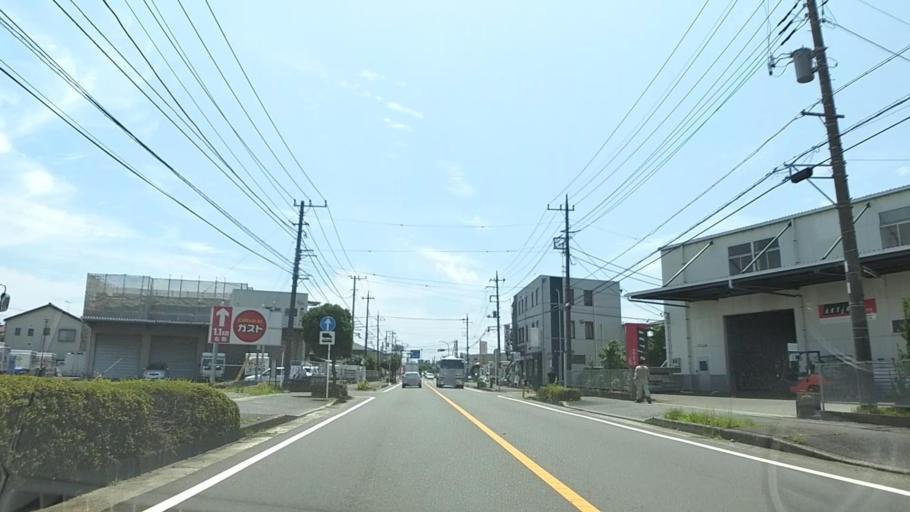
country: JP
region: Kanagawa
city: Atsugi
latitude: 35.4046
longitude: 139.3828
